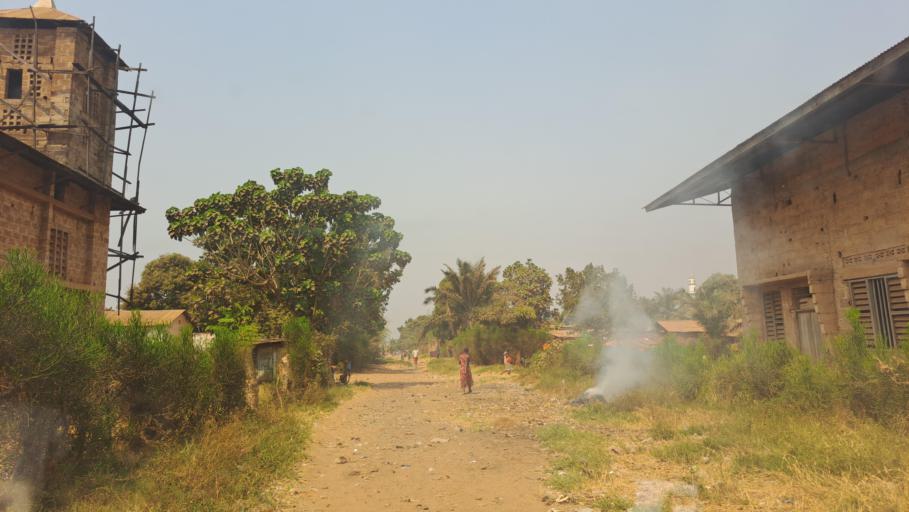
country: CD
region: Kasai-Oriental
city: Mbuji-Mayi
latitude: -6.1255
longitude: 23.6124
